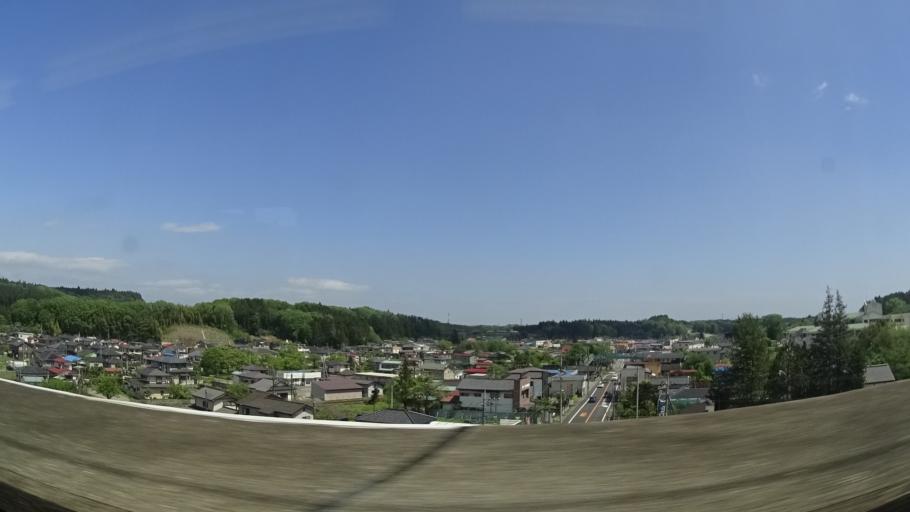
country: JP
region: Tochigi
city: Yaita
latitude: 36.7579
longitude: 139.9423
